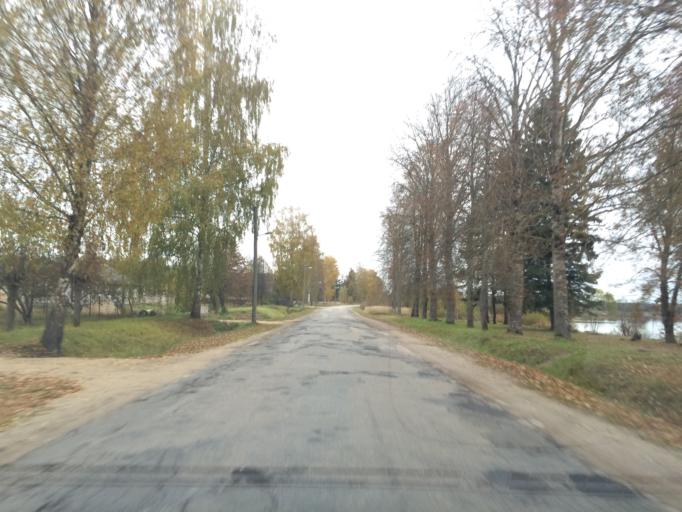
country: LV
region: Plavinu
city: Plavinas
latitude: 56.6167
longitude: 25.7615
